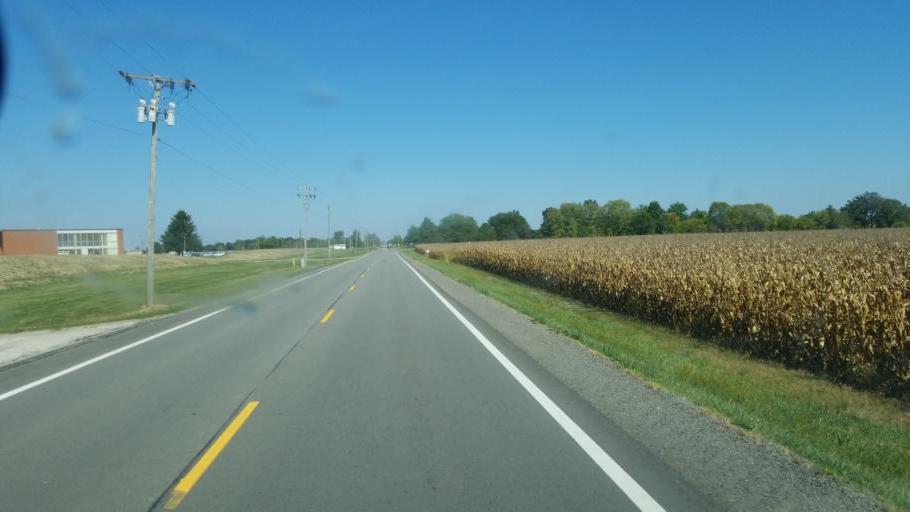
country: US
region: Ohio
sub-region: Marion County
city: Marion
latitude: 40.6087
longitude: -83.0320
